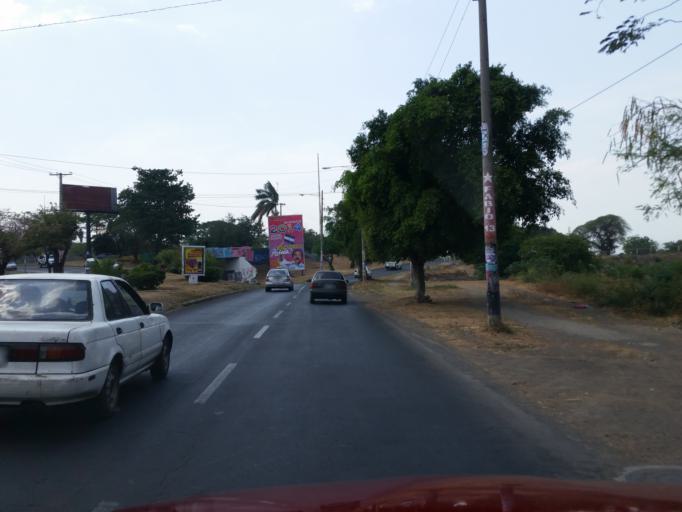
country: NI
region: Managua
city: Managua
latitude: 12.1357
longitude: -86.2684
